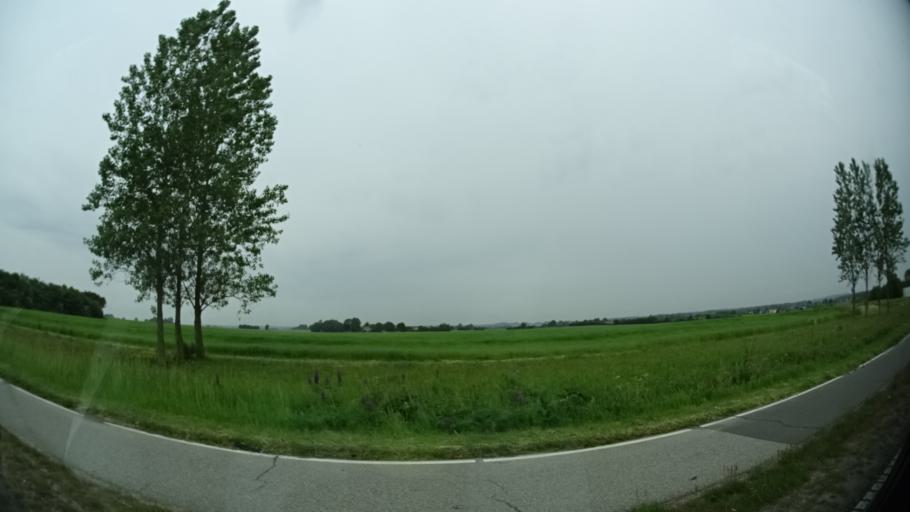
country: DK
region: Central Jutland
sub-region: Arhus Kommune
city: Hjortshoj
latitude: 56.2231
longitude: 10.2880
